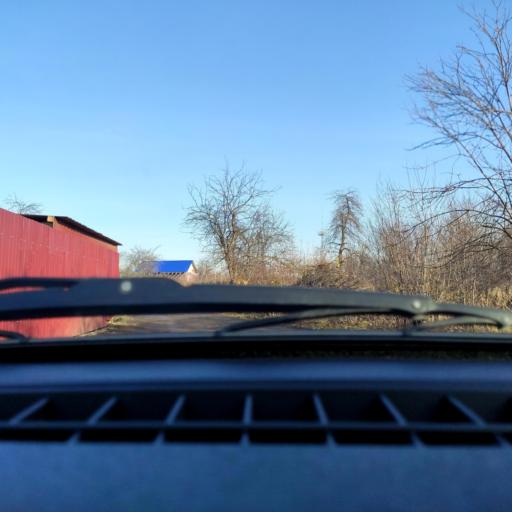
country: RU
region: Bashkortostan
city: Ufa
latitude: 54.8277
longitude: 56.1012
